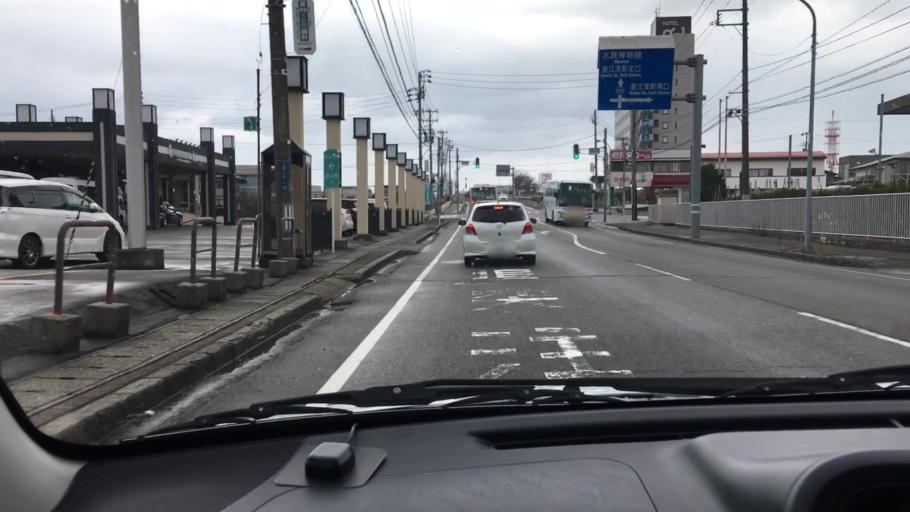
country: JP
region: Niigata
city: Joetsu
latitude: 37.1646
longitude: 138.2372
